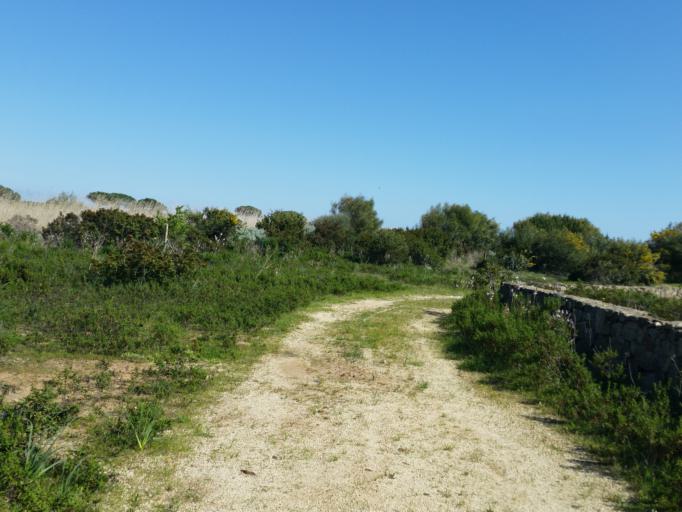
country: IT
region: Sardinia
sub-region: Provincia di Olbia-Tempio
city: Budoni
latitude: 40.7189
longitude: 9.7111
